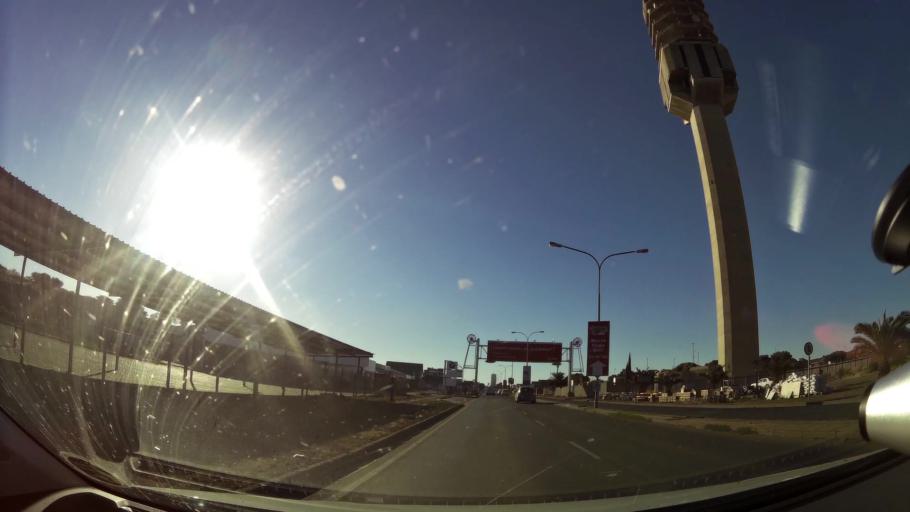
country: ZA
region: Northern Cape
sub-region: Frances Baard District Municipality
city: Kimberley
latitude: -28.7442
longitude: 24.7481
